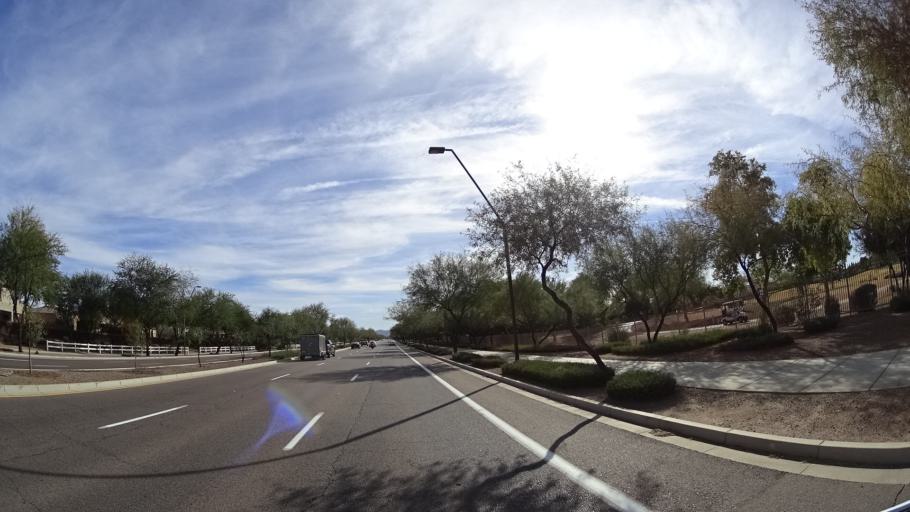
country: US
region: Arizona
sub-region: Maricopa County
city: Queen Creek
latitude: 33.2606
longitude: -111.6861
